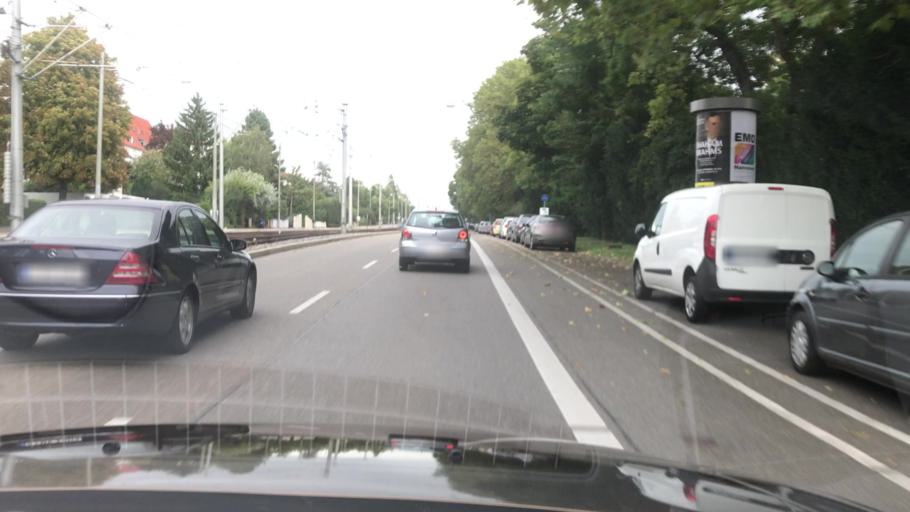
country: DE
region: Baden-Wuerttemberg
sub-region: Regierungsbezirk Stuttgart
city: Fellbach
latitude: 48.8086
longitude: 9.2446
